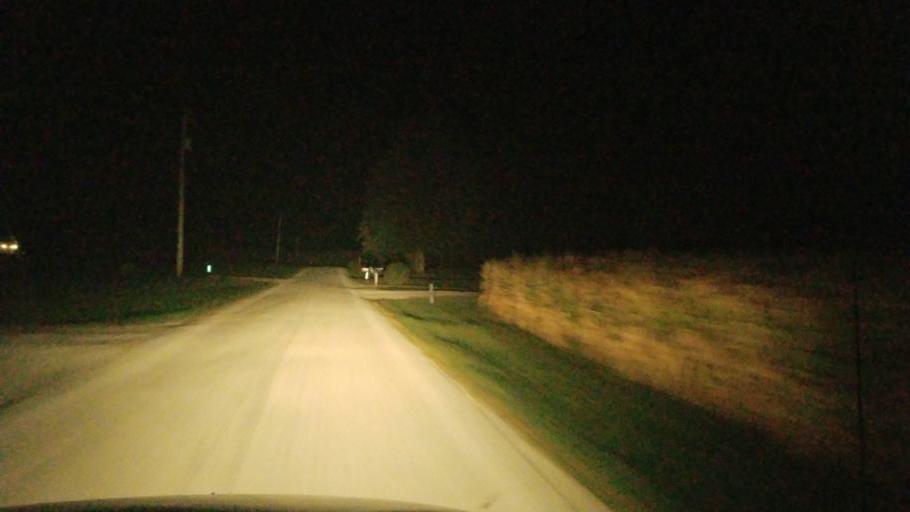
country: US
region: Ohio
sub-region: Highland County
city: Leesburg
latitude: 39.3037
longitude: -83.5626
